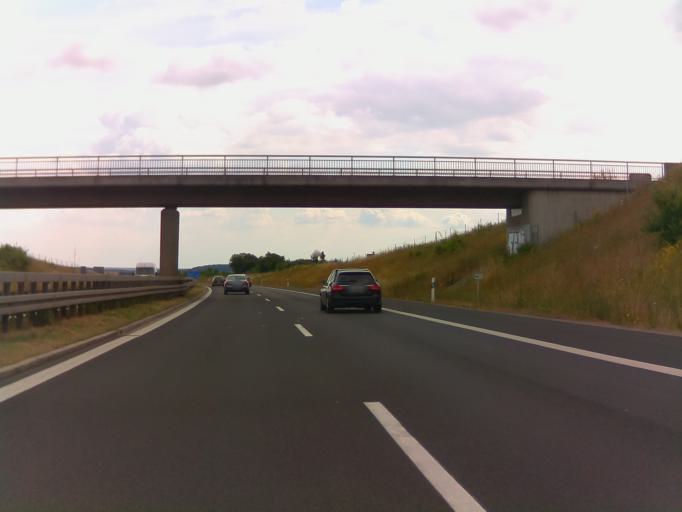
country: DE
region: Bavaria
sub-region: Regierungsbezirk Unterfranken
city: Oerlenbach
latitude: 50.1399
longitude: 10.1525
